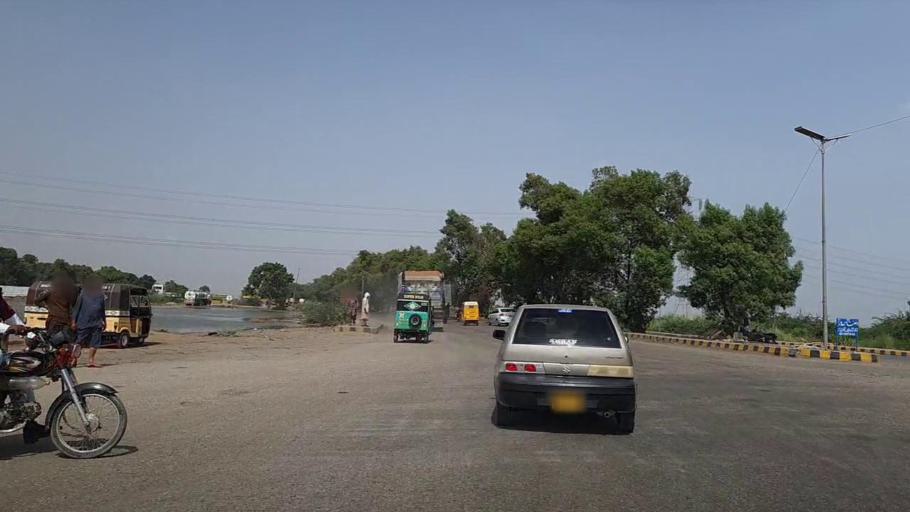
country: PK
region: Sindh
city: Malir Cantonment
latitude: 24.8664
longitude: 67.3003
